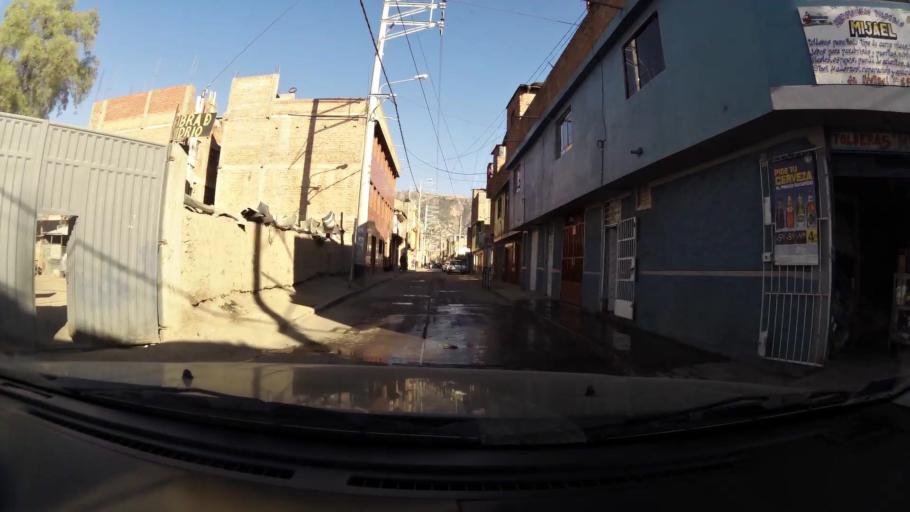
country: PE
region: Ayacucho
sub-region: Provincia de Huamanga
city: Ayacucho
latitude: -13.1596
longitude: -74.2188
